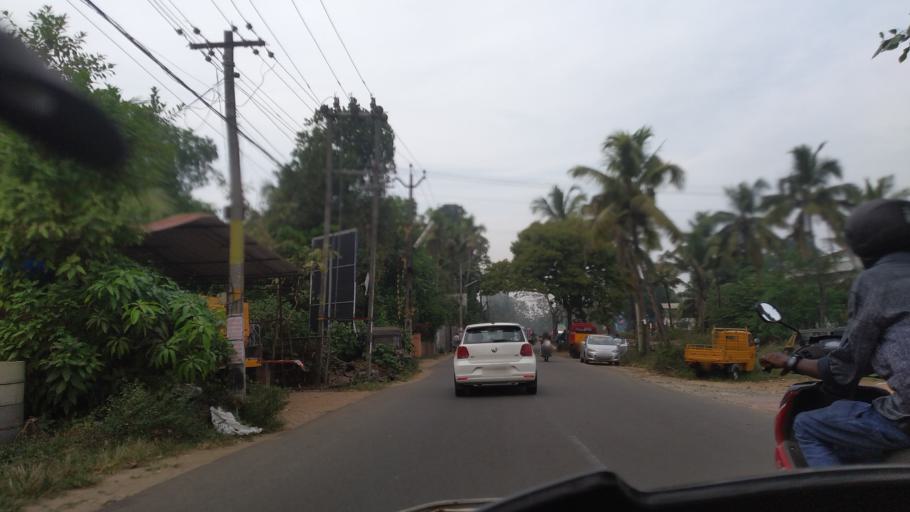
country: IN
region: Kerala
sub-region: Ernakulam
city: Elur
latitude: 10.1078
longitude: 76.2617
